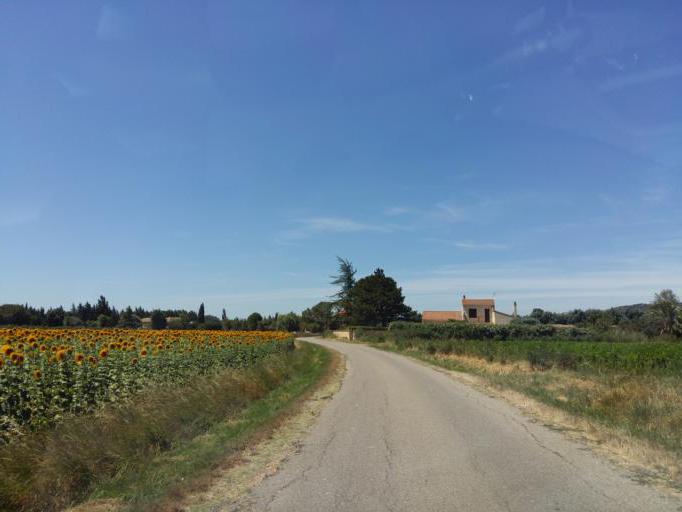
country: FR
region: Provence-Alpes-Cote d'Azur
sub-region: Departement du Vaucluse
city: Piolenc
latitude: 44.1824
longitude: 4.7503
